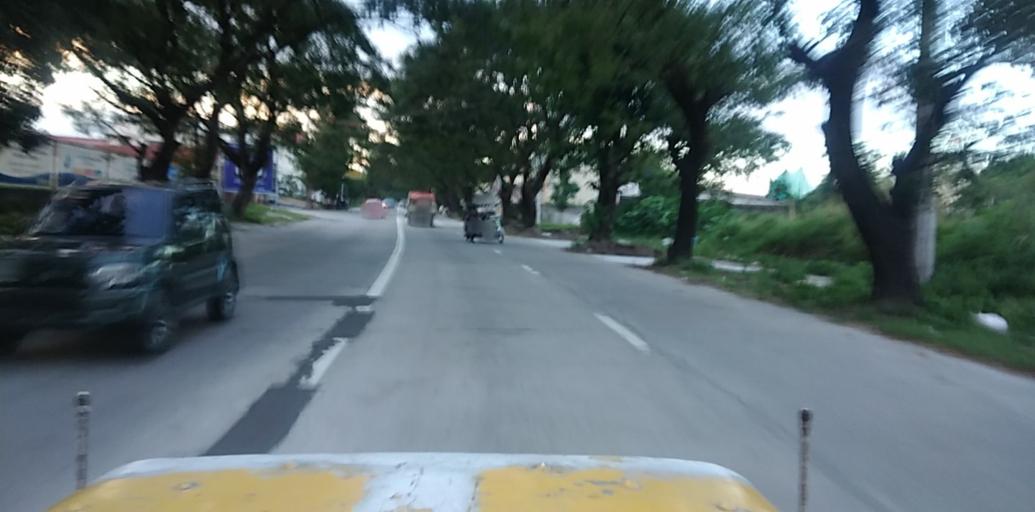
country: PH
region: Central Luzon
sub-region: Province of Pampanga
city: Calibutbut
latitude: 15.1258
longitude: 120.5847
